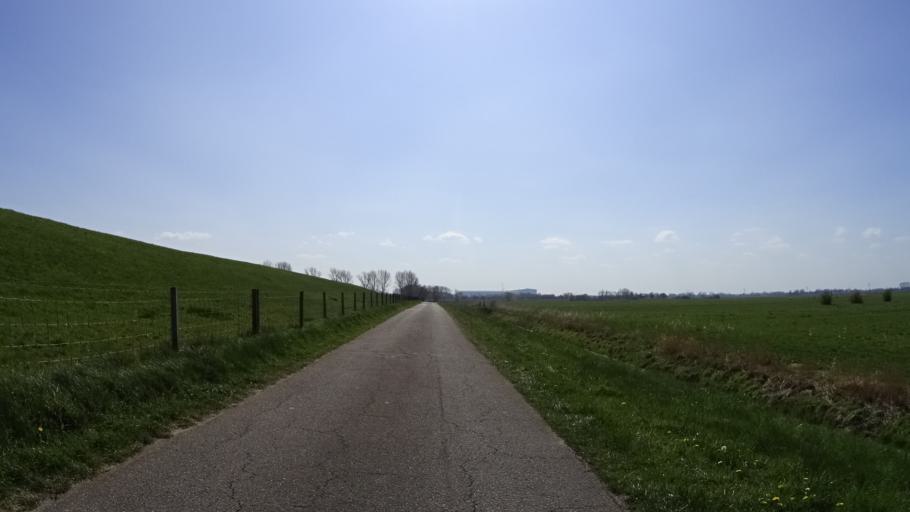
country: DE
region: Lower Saxony
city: Weener
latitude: 53.1326
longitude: 7.3626
